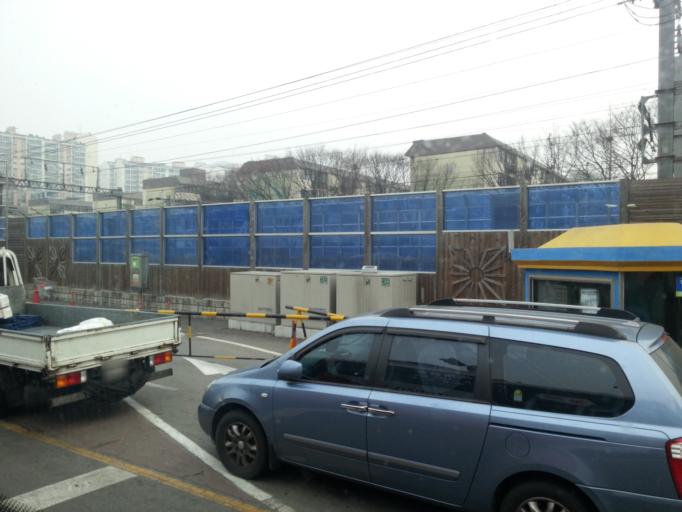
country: KR
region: Gyeonggi-do
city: Anyang-si
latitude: 37.3970
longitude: 126.9265
